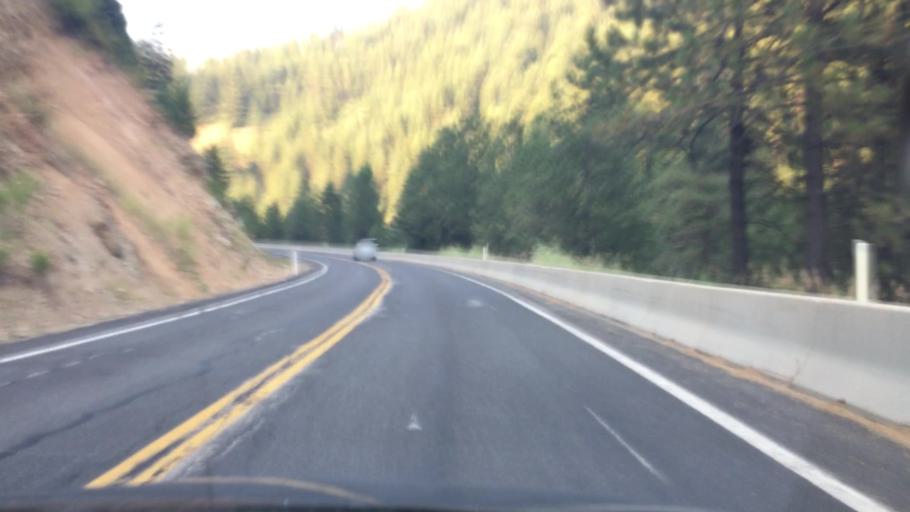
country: US
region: Idaho
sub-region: Valley County
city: Cascade
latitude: 44.2618
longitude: -116.0683
